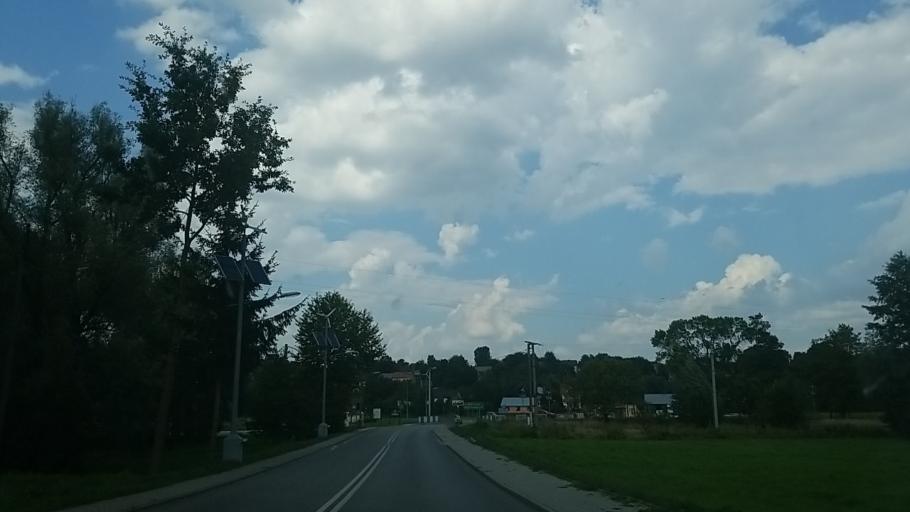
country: PL
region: Lublin Voivodeship
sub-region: Powiat bilgorajski
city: Goraj
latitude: 50.7227
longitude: 22.6689
